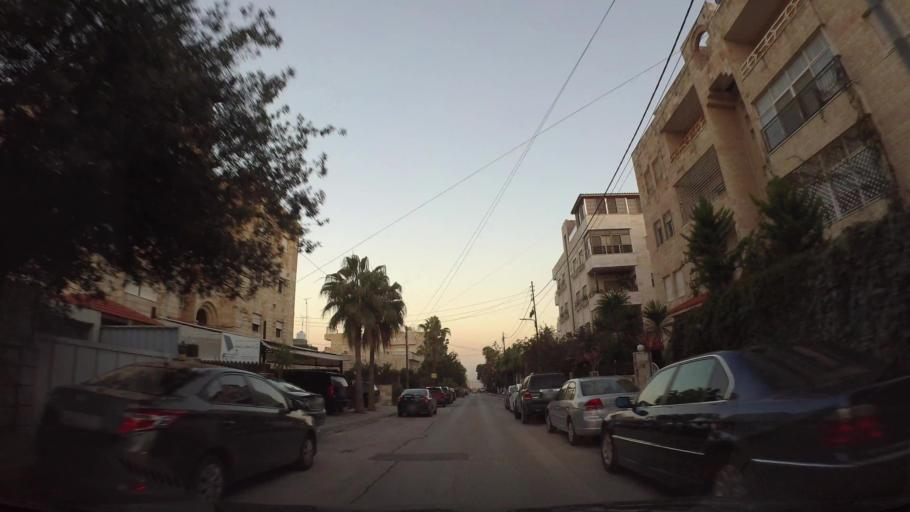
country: JO
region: Amman
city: Al Jubayhah
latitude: 31.9912
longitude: 35.8883
